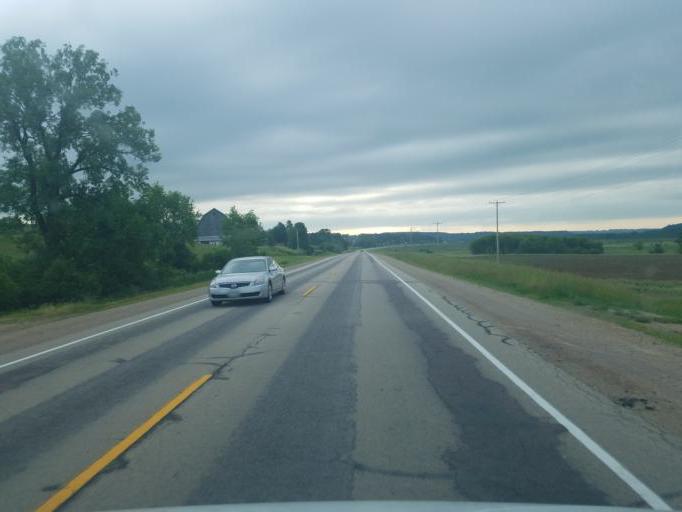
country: US
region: Wisconsin
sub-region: Vernon County
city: Hillsboro
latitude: 43.6774
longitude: -90.3063
